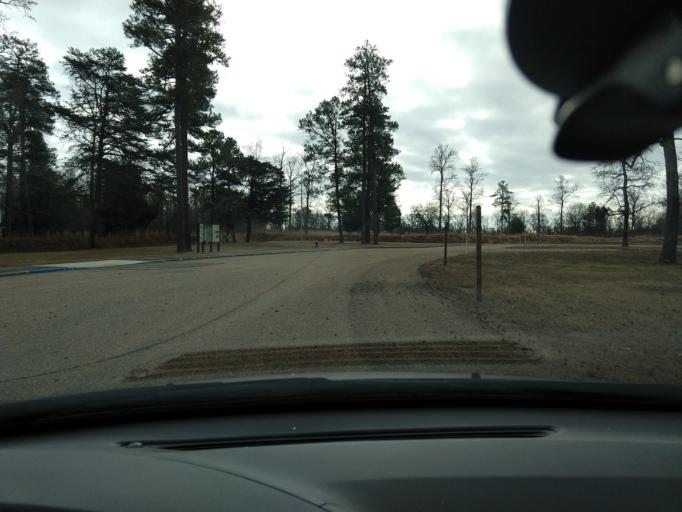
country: US
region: Virginia
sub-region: Chesterfield County
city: Bellwood
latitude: 37.4286
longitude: -77.3734
